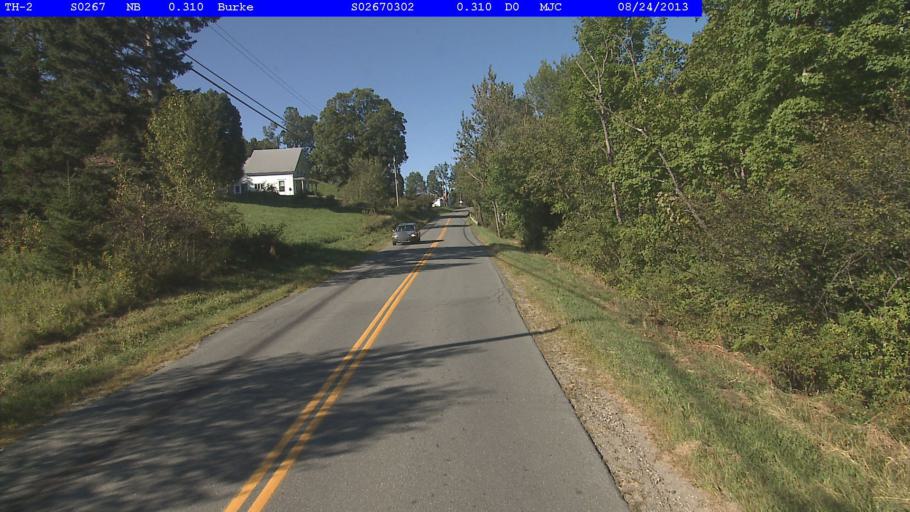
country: US
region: Vermont
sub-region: Caledonia County
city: Lyndonville
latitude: 44.5916
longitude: -71.9452
